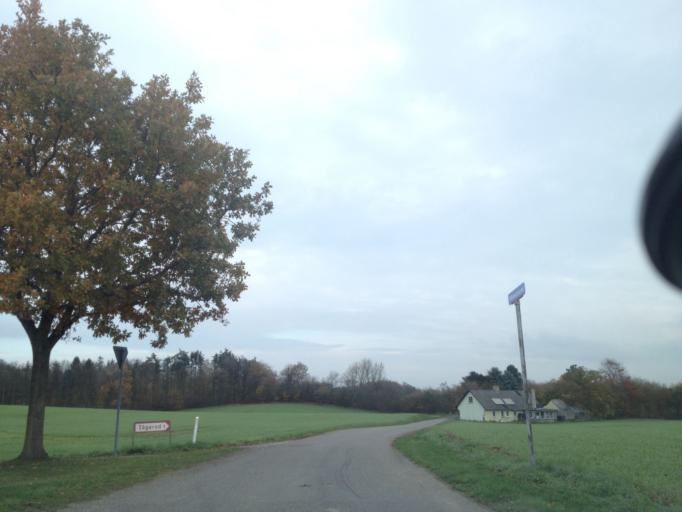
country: DK
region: South Denmark
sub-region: Assens Kommune
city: Vissenbjerg
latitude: 55.4221
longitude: 10.1651
